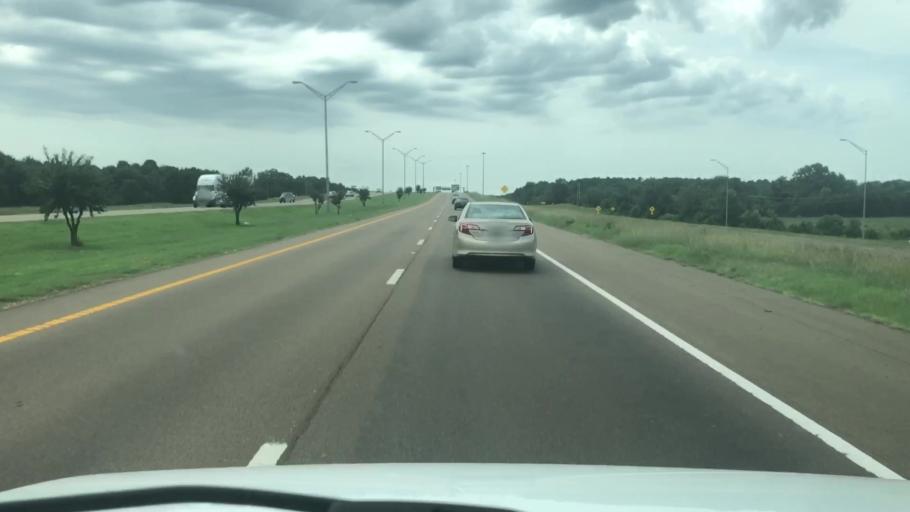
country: US
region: Texas
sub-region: Bowie County
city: Wake Village
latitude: 33.4067
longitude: -94.0977
